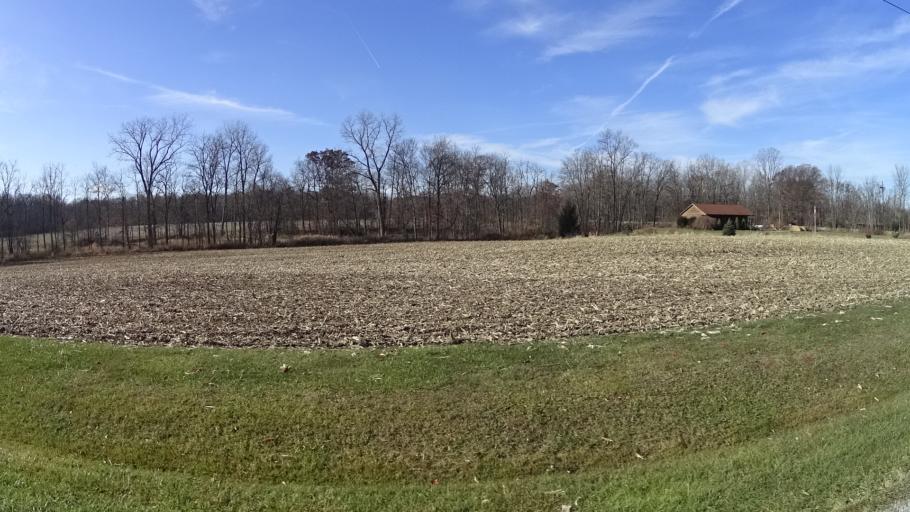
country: US
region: Ohio
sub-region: Lorain County
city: Wellington
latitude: 41.0918
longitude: -82.2009
